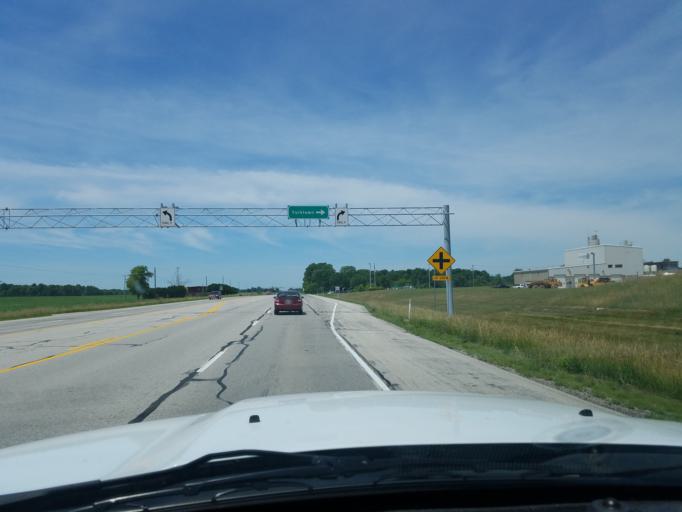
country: US
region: Indiana
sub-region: Delaware County
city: Yorktown
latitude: 40.1137
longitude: -85.4969
